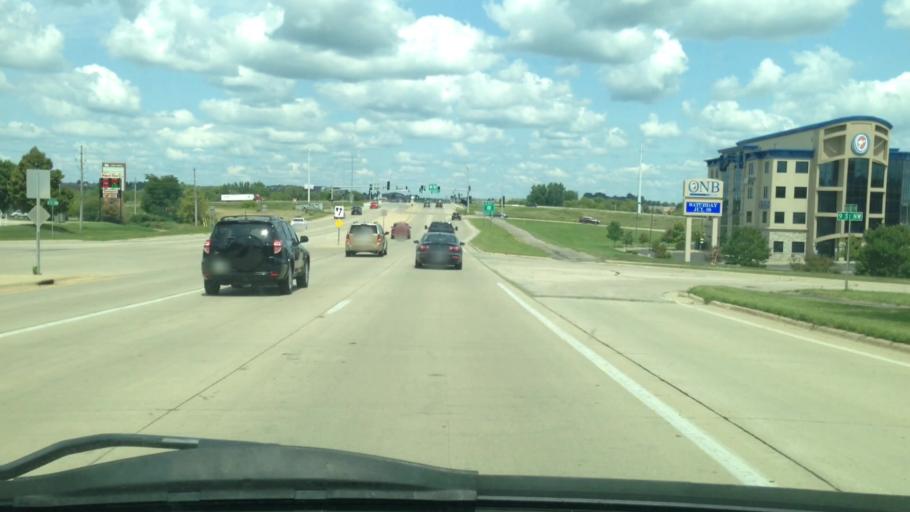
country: US
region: Minnesota
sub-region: Olmsted County
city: Rochester
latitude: 44.0340
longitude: -92.5166
